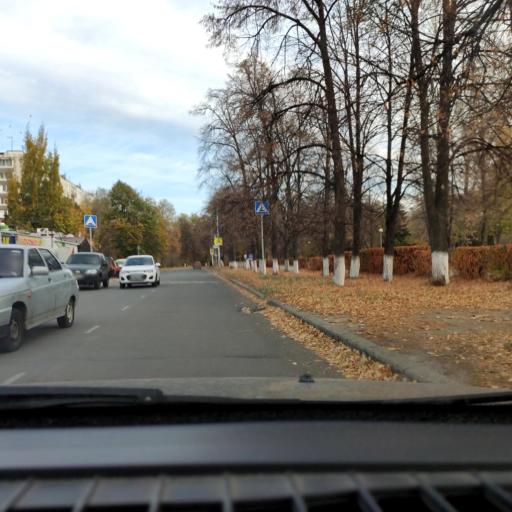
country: RU
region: Samara
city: Tol'yatti
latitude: 53.5105
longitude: 49.2616
